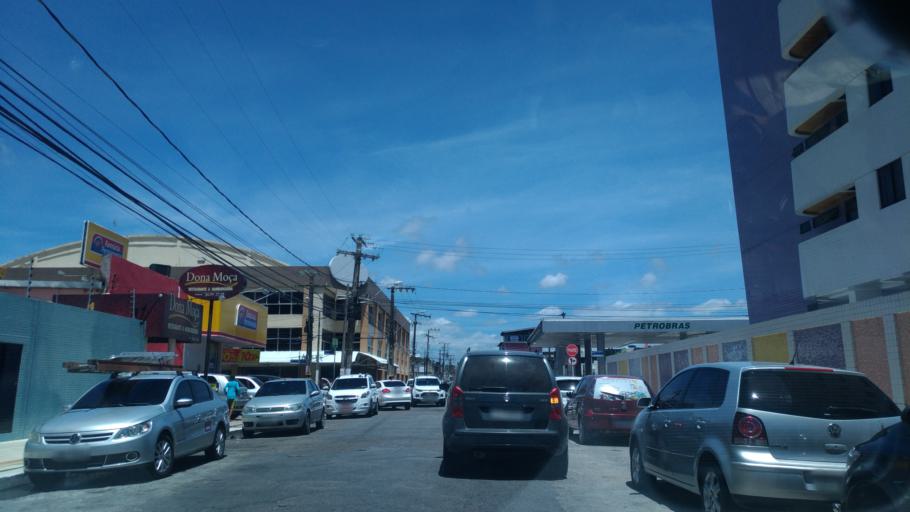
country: BR
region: Alagoas
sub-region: Maceio
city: Maceio
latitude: -9.6646
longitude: -35.7107
